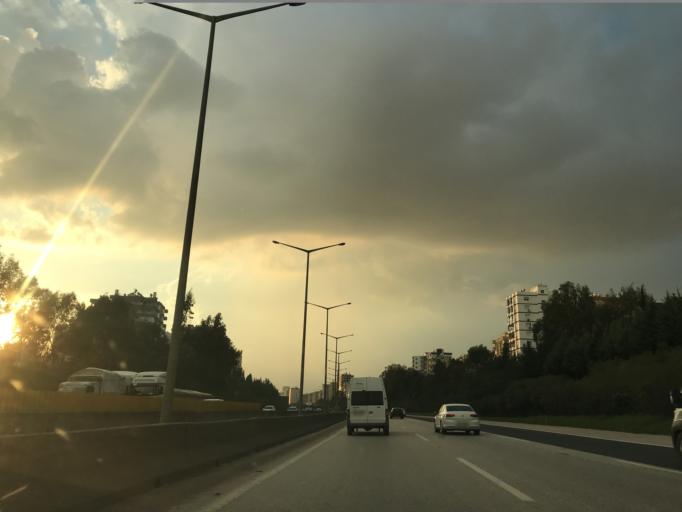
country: TR
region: Adana
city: Adana
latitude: 37.0319
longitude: 35.3077
